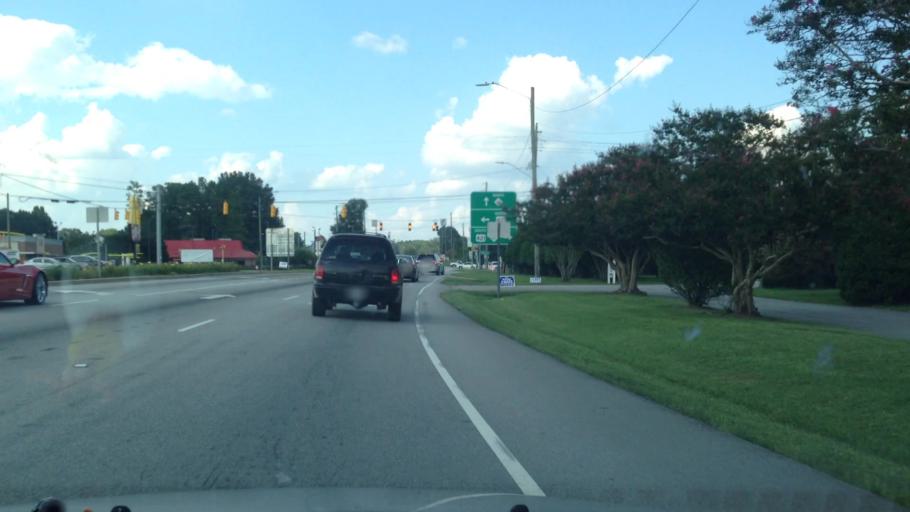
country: US
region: North Carolina
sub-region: Harnett County
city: Lillington
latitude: 35.4172
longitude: -78.8042
